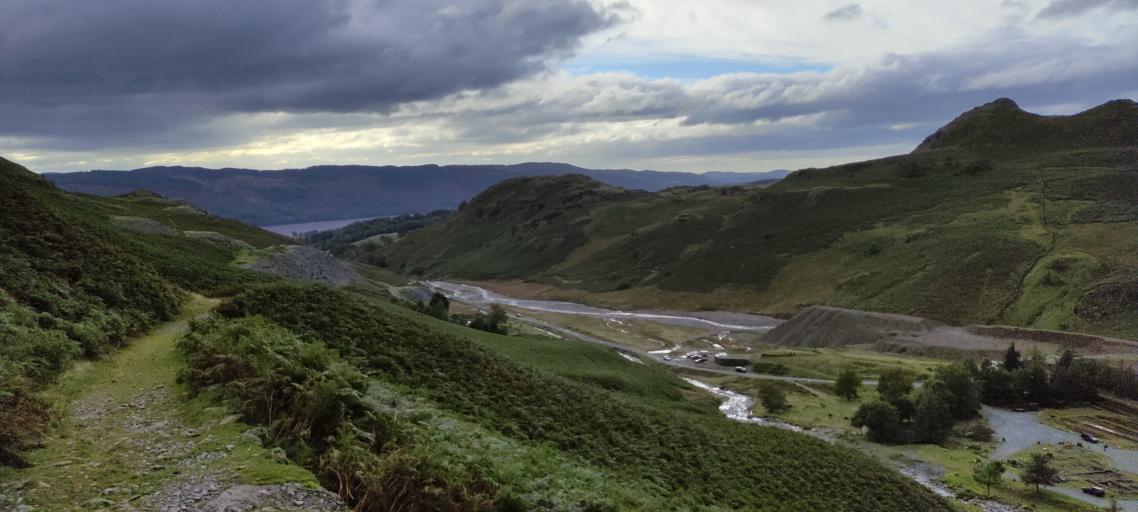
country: GB
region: England
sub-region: Cumbria
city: Ambleside
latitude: 54.3806
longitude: -3.0939
